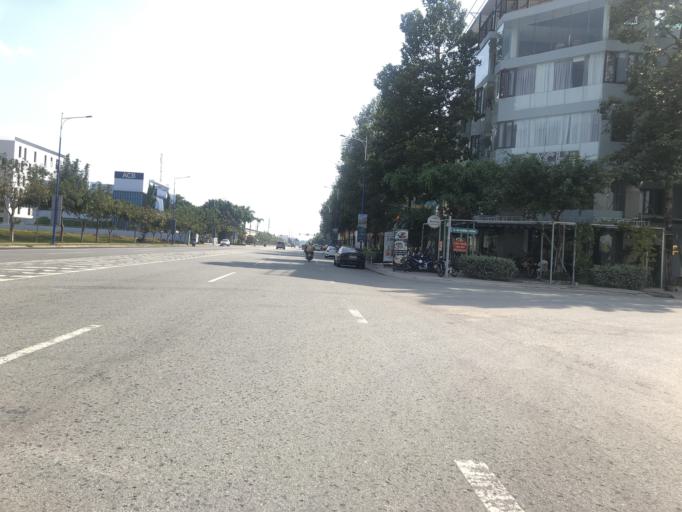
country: VN
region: Binh Duong
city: Thu Dau Mot
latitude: 11.0729
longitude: 106.6825
